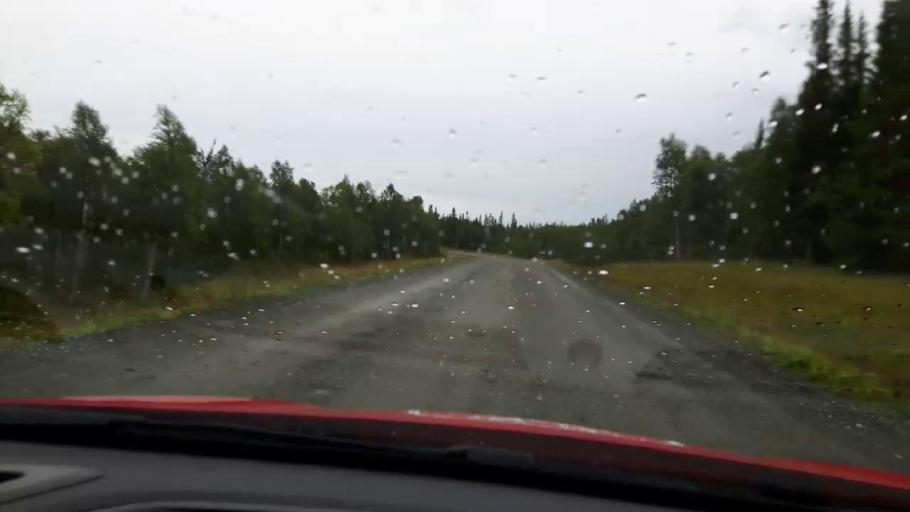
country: NO
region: Nord-Trondelag
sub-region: Meraker
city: Meraker
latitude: 63.5619
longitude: 12.2919
